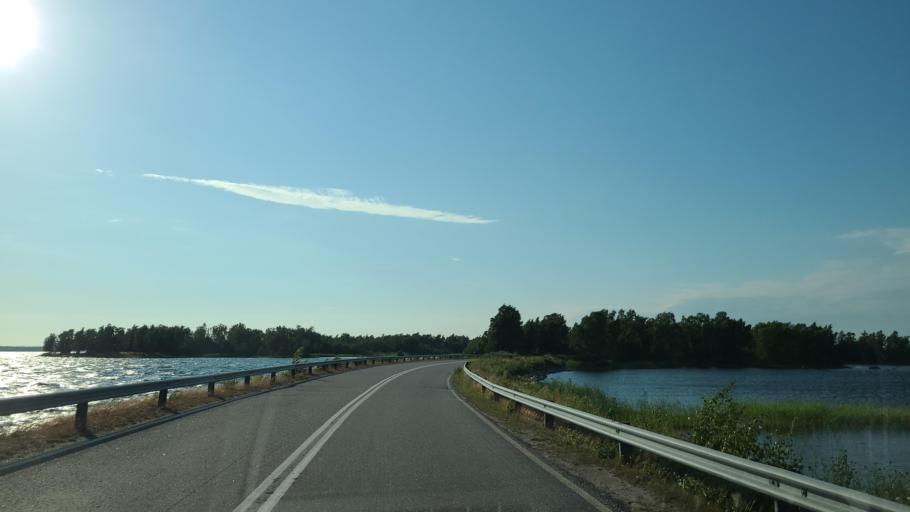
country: FI
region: Ostrobothnia
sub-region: Vaasa
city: Replot
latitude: 63.2815
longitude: 21.3384
